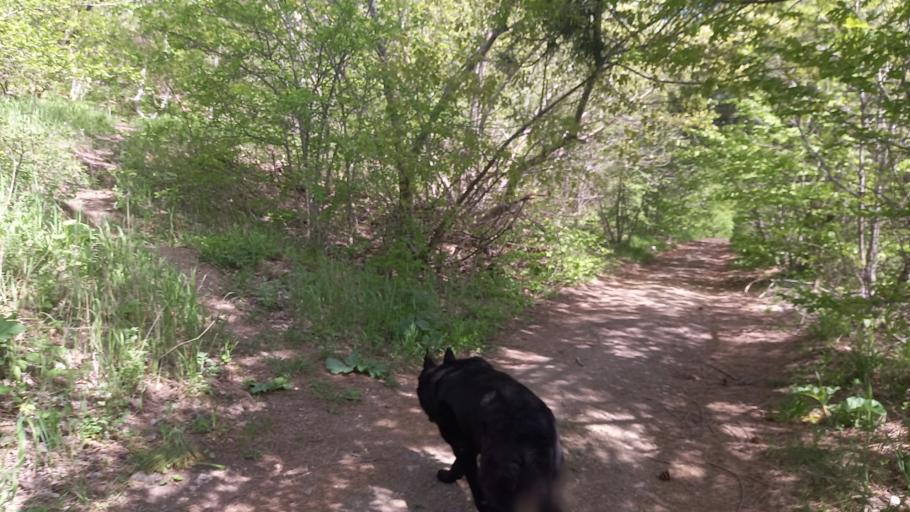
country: RU
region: Stavropol'skiy
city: Pyatigorsk
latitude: 44.0881
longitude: 43.0294
